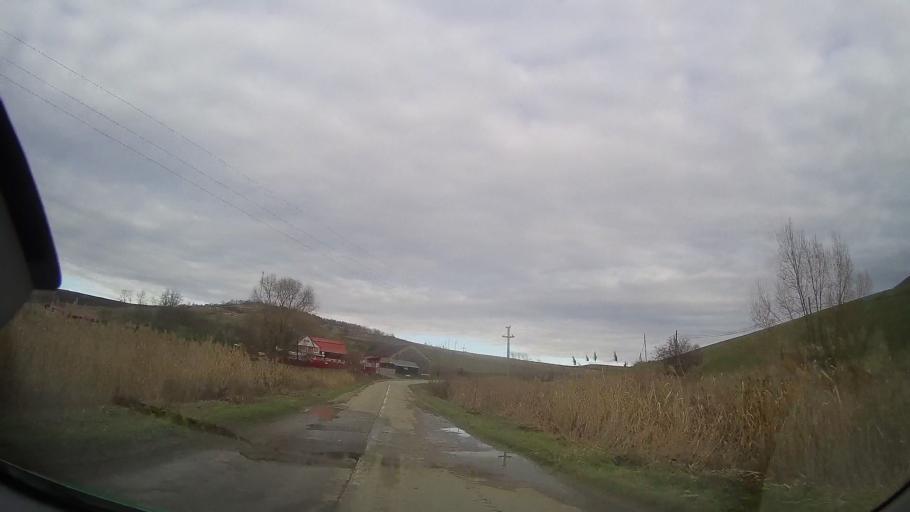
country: RO
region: Bistrita-Nasaud
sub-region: Comuna Micestii de Campie
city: Micestii de Campie
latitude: 46.8446
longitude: 24.3000
